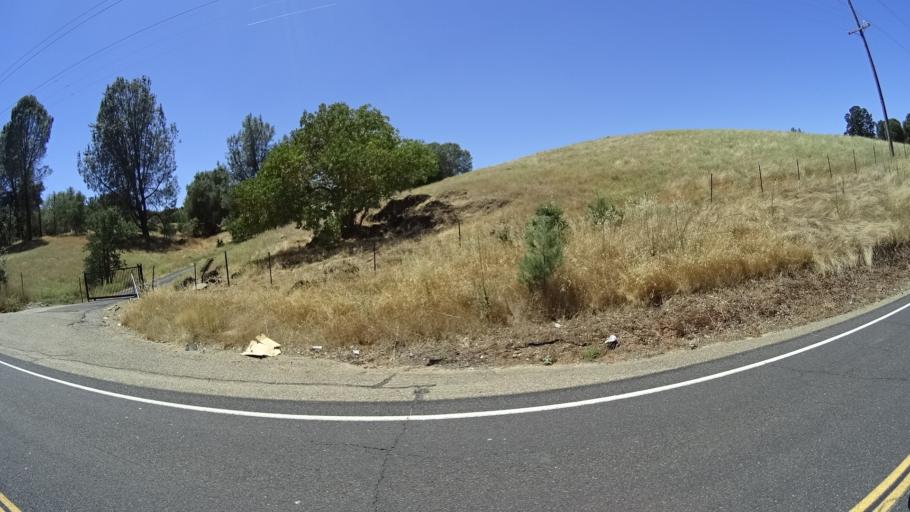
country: US
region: California
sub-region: Calaveras County
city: San Andreas
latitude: 38.1956
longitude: -120.6923
